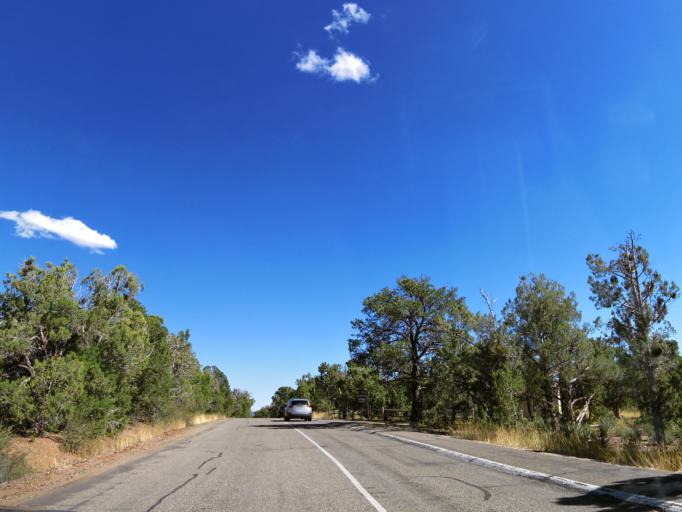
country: US
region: Colorado
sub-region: Montezuma County
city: Cortez
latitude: 37.1658
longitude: -108.4879
